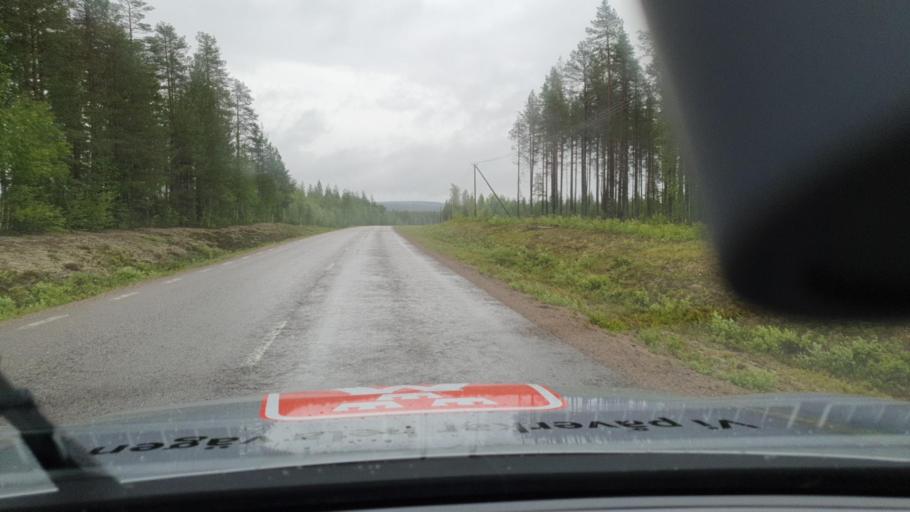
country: SE
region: Norrbotten
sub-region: Overkalix Kommun
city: OEverkalix
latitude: 66.4459
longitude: 23.1600
